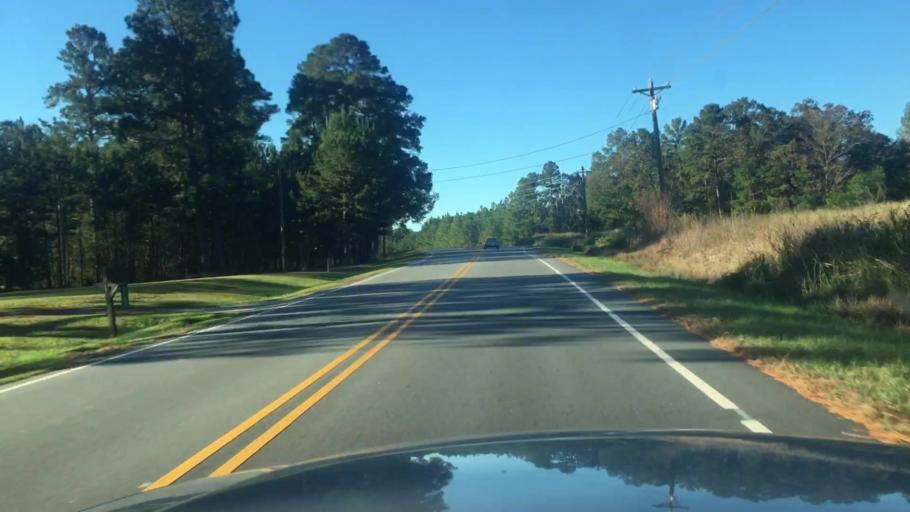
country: US
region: North Carolina
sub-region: Harnett County
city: Walkertown
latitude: 35.2666
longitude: -78.9213
